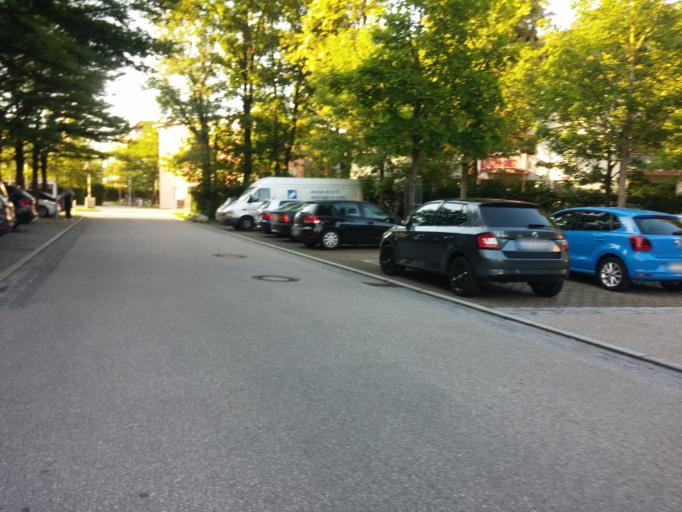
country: DE
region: Bavaria
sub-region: Upper Bavaria
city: Feldkirchen
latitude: 48.1475
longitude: 11.7365
